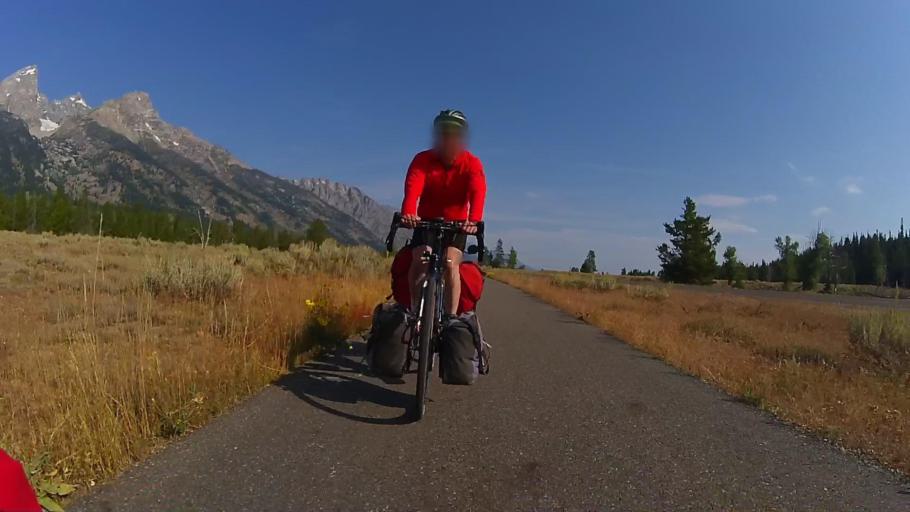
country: US
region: Wyoming
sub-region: Teton County
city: Moose Wilson Road
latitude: 43.7147
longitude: -110.7280
